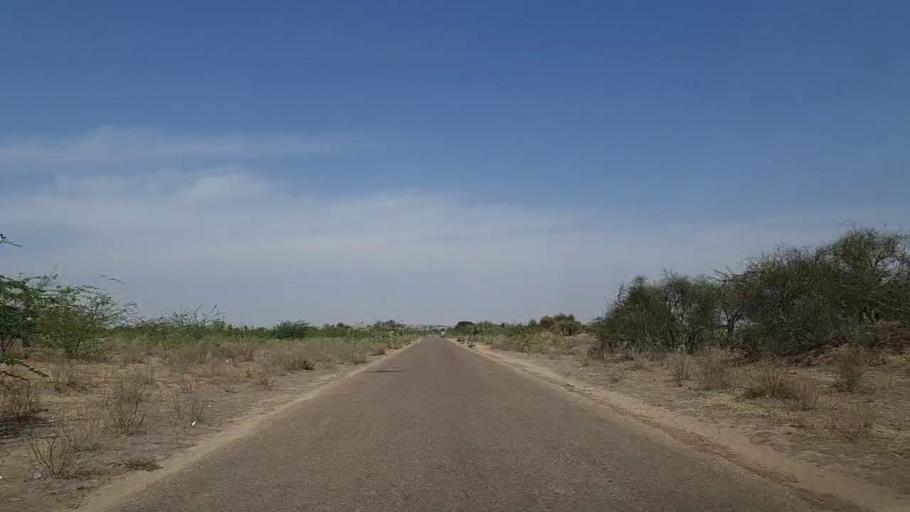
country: PK
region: Sindh
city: Nabisar
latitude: 25.0831
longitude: 69.9857
